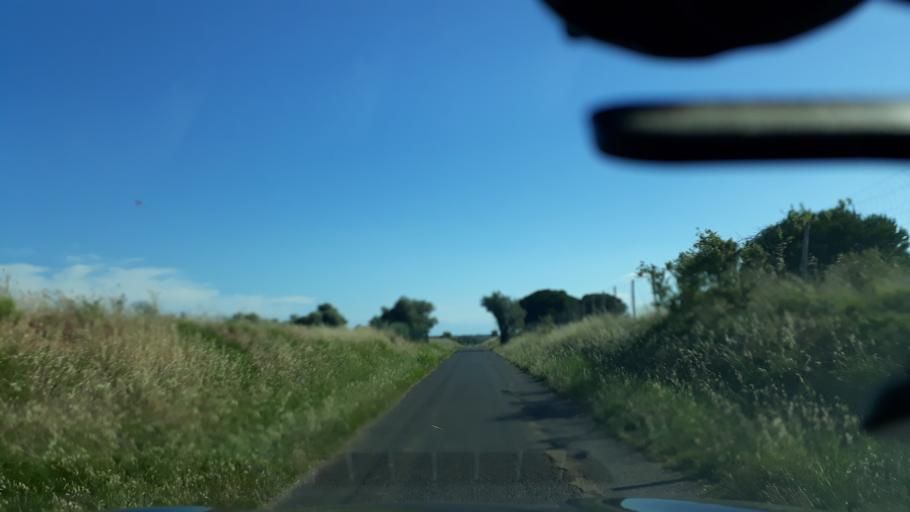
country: FR
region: Languedoc-Roussillon
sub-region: Departement de l'Herault
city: Marseillan
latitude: 43.3476
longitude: 3.5150
